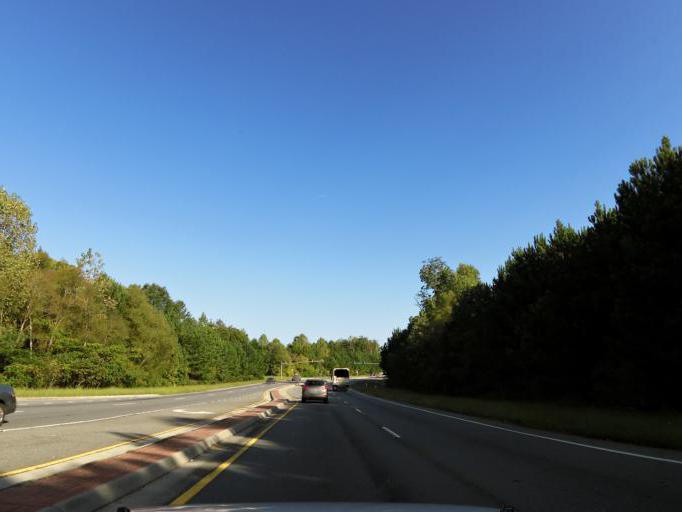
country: US
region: Georgia
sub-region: Cobb County
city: Powder Springs
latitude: 33.8696
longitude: -84.6336
